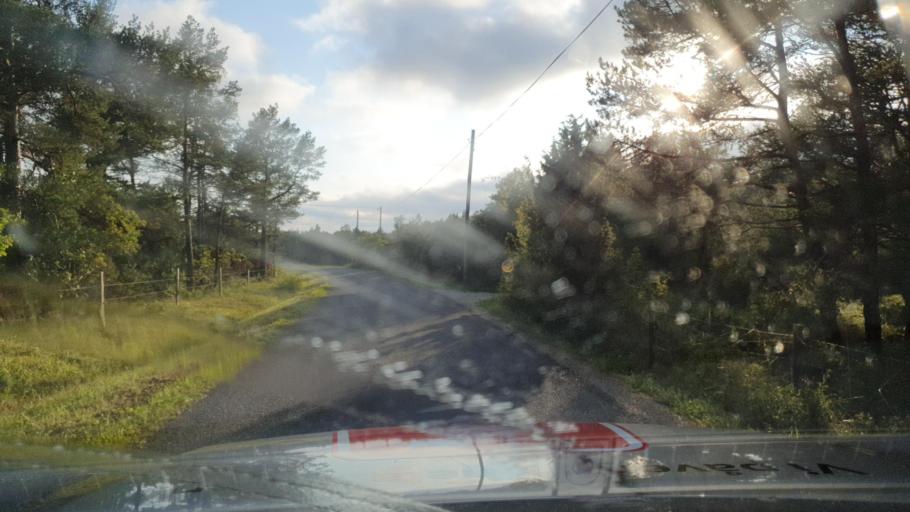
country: SE
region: Gotland
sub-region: Gotland
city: Klintehamn
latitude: 57.4483
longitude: 18.1702
